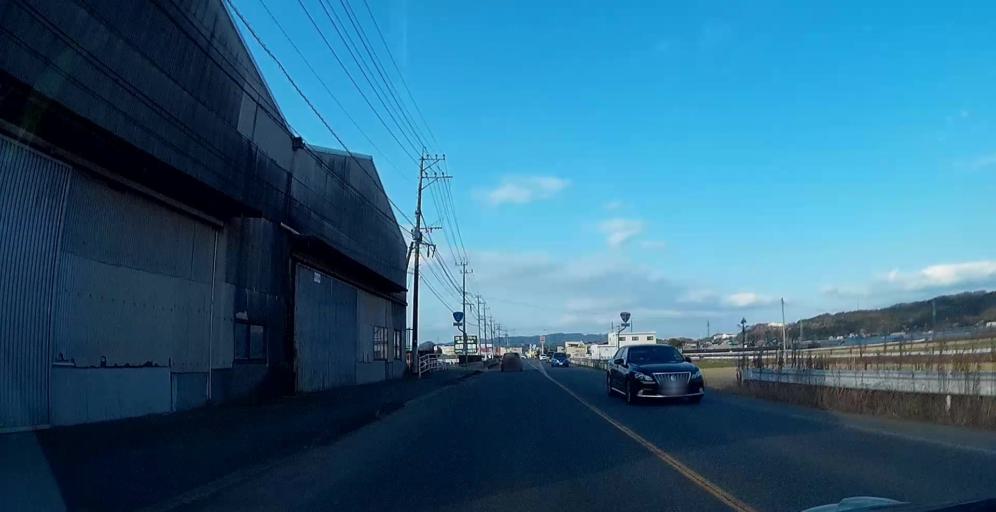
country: JP
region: Kumamoto
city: Matsubase
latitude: 32.6139
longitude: 130.7046
